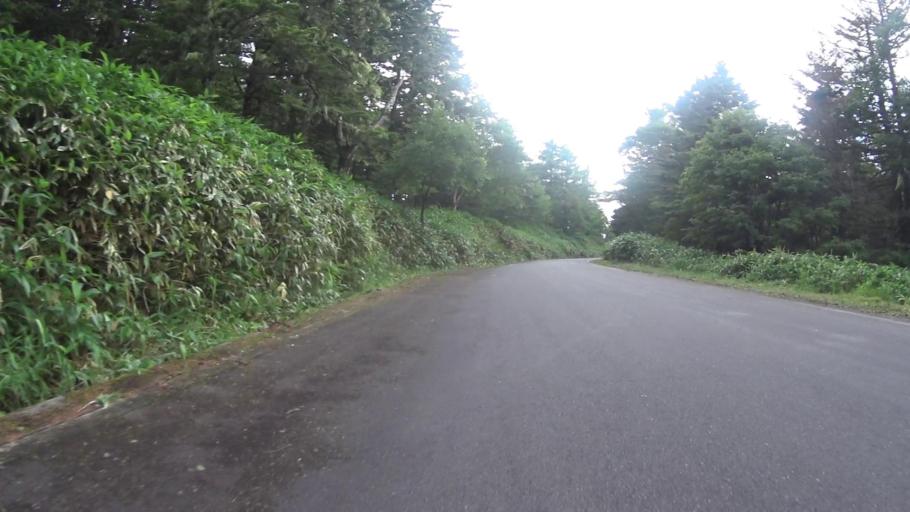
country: JP
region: Nagano
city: Saku
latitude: 36.1139
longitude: 138.3303
